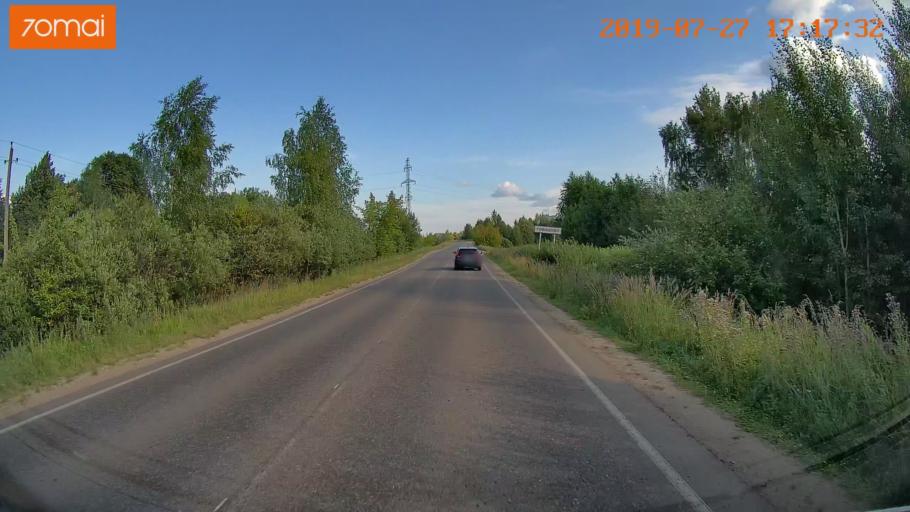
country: RU
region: Ivanovo
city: Novo-Talitsy
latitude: 57.0364
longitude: 40.8957
